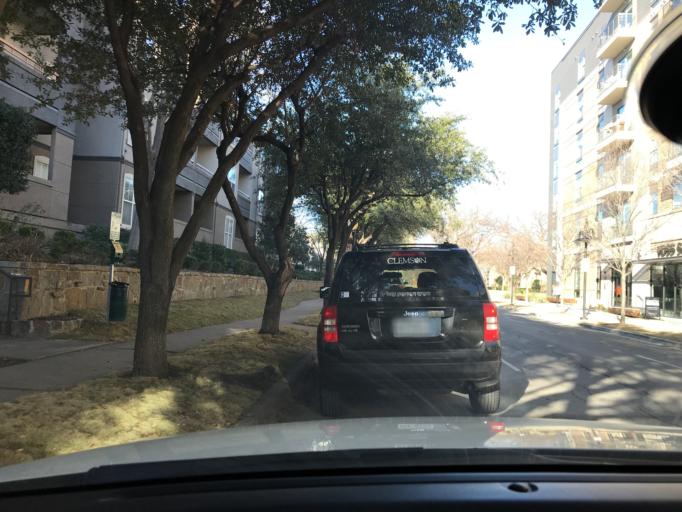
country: US
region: Texas
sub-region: Dallas County
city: Highland Park
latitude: 32.8239
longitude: -96.7869
